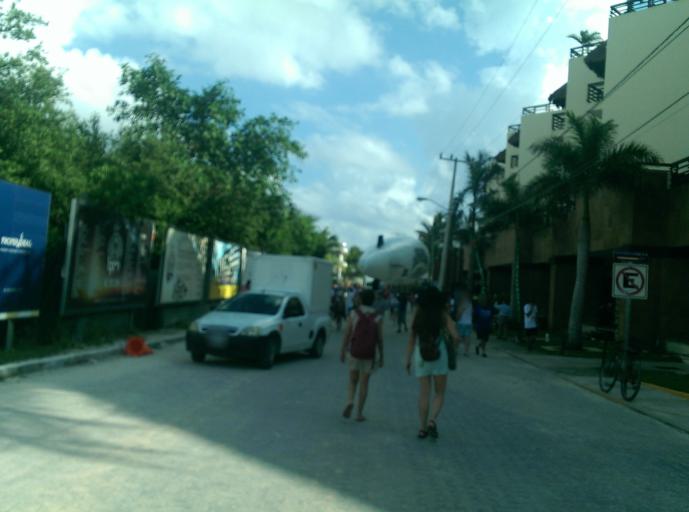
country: MX
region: Quintana Roo
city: Playa del Carmen
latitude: 20.6316
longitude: -87.0664
